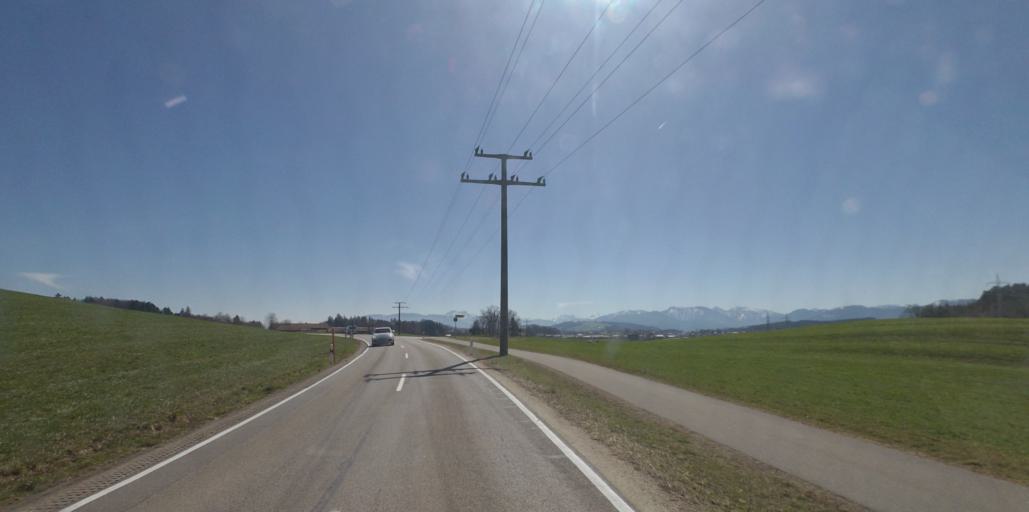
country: DE
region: Bavaria
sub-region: Upper Bavaria
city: Nussdorf
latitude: 47.8881
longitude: 12.6153
